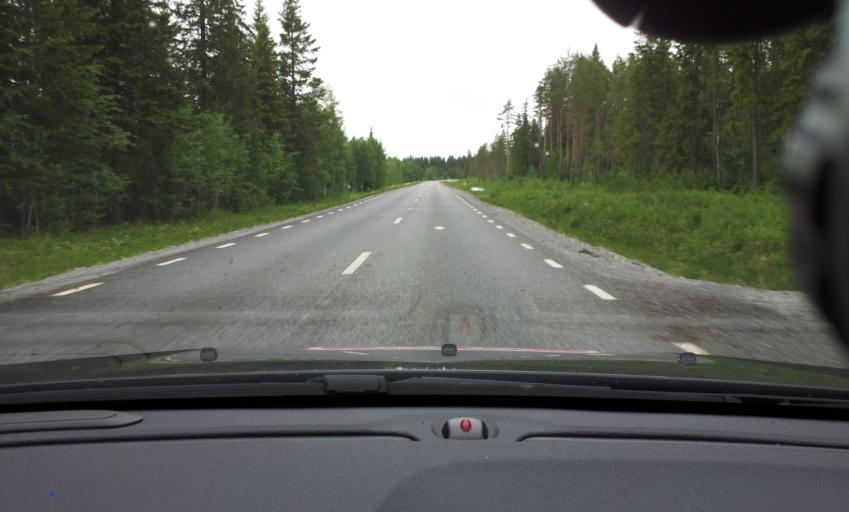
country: SE
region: Jaemtland
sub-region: OEstersunds Kommun
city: Lit
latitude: 63.6801
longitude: 14.6806
